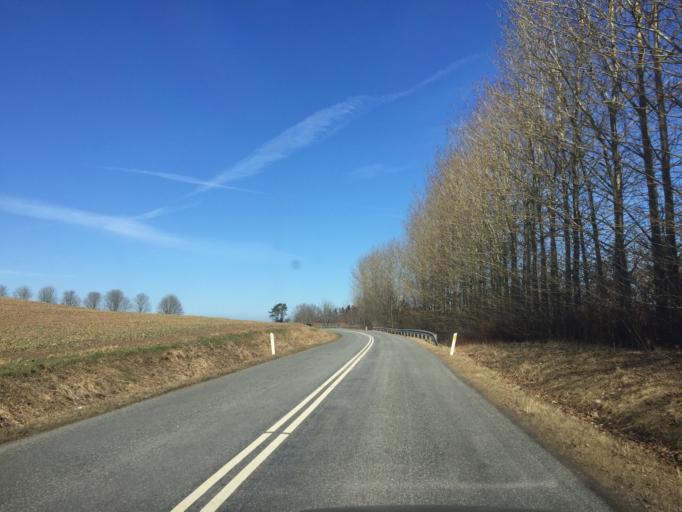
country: DK
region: Capital Region
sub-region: Helsingor Kommune
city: Hornbaek
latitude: 56.0590
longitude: 12.3817
